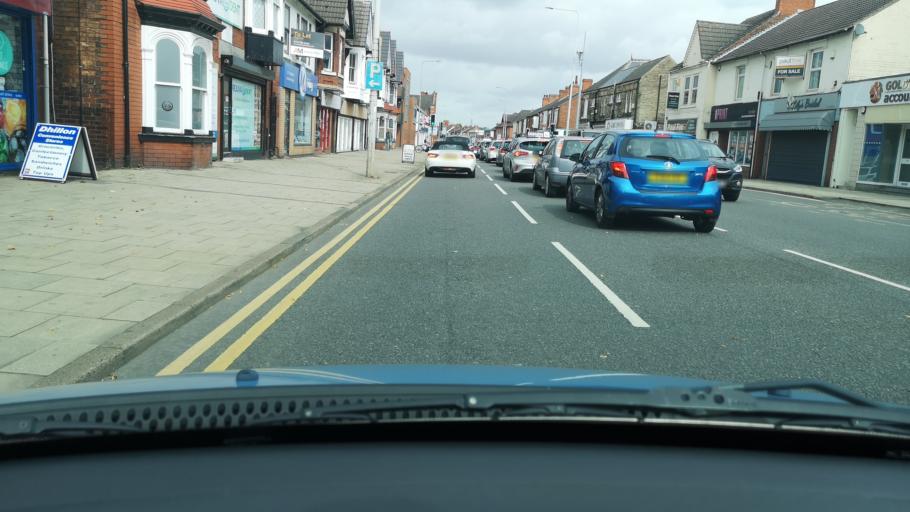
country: GB
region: England
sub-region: North Lincolnshire
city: Scunthorpe
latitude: 53.5892
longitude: -0.6540
